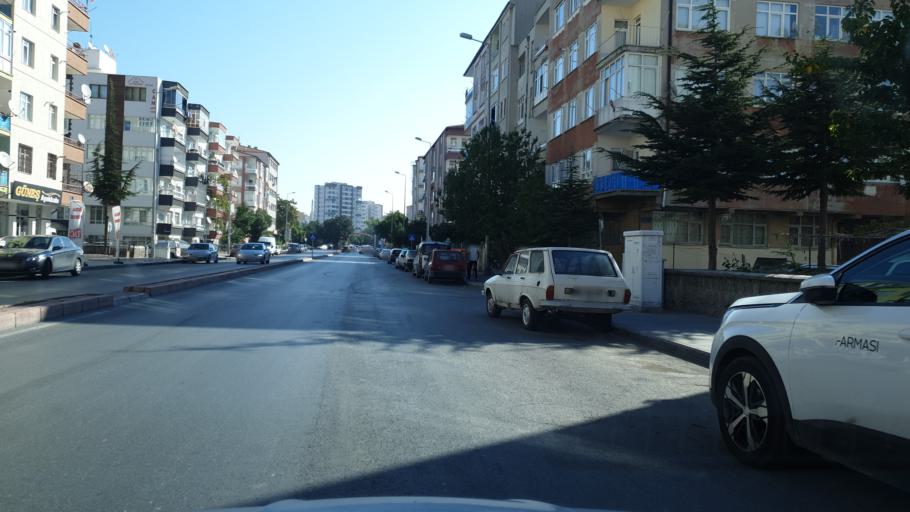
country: TR
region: Kayseri
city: Kayseri
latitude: 38.7387
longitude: 35.4891
